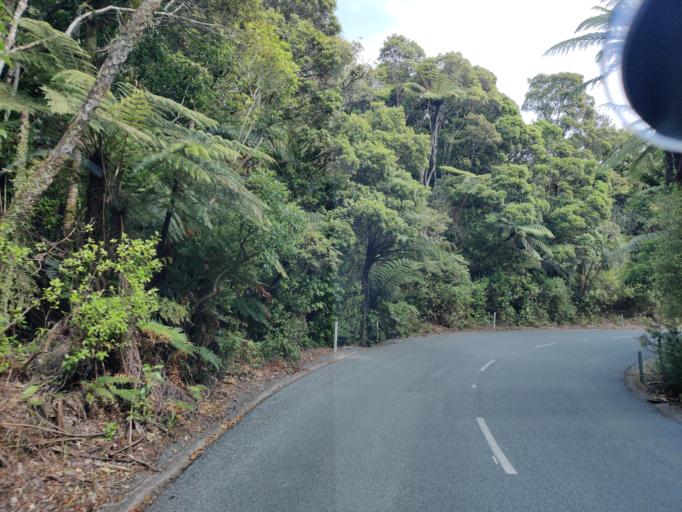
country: NZ
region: Northland
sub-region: Kaipara District
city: Dargaville
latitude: -35.6434
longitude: 173.5599
